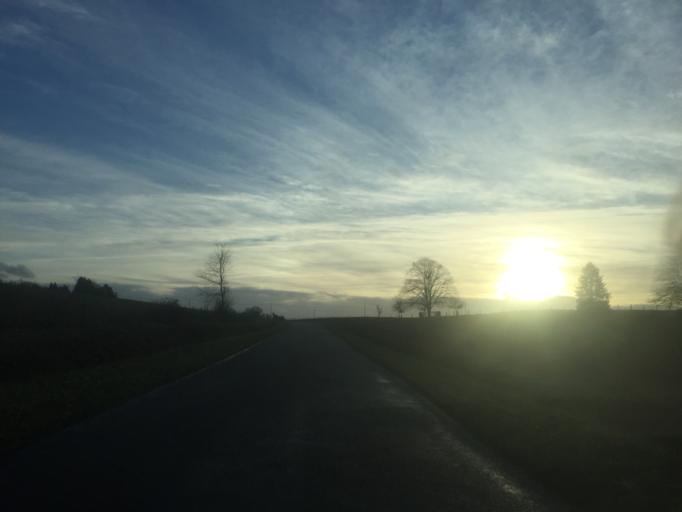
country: FR
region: Franche-Comte
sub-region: Departement du Jura
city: Dampierre
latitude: 47.1290
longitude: 5.7123
